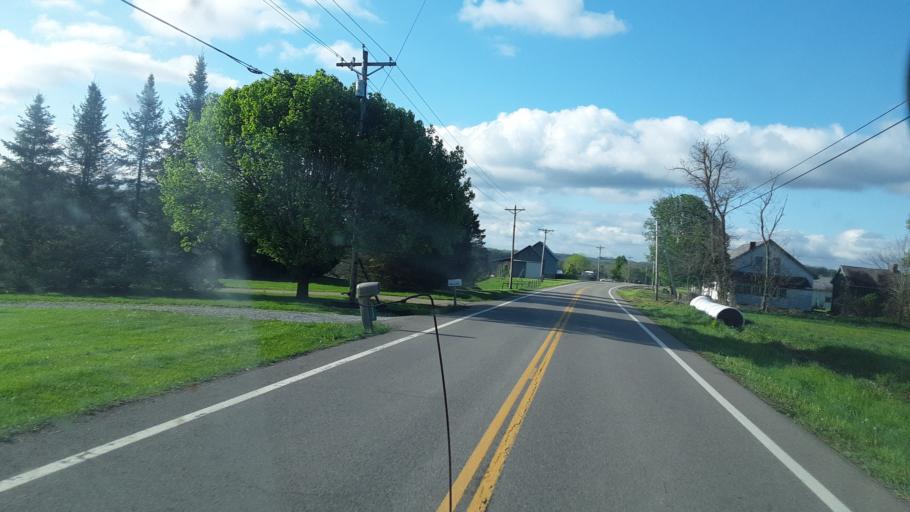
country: US
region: Ohio
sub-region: Muskingum County
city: New Concord
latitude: 39.9230
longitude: -81.6786
